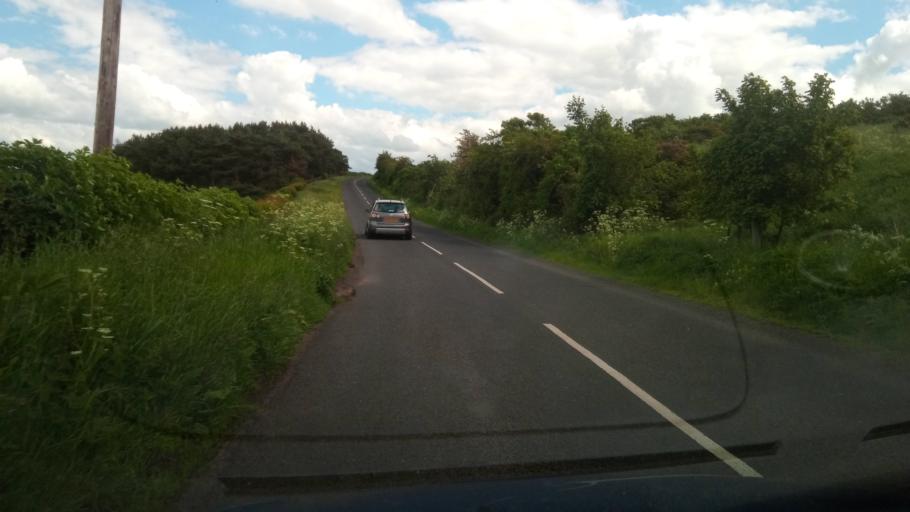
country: GB
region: Scotland
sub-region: The Scottish Borders
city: Coldstream
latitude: 55.6037
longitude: -2.2716
